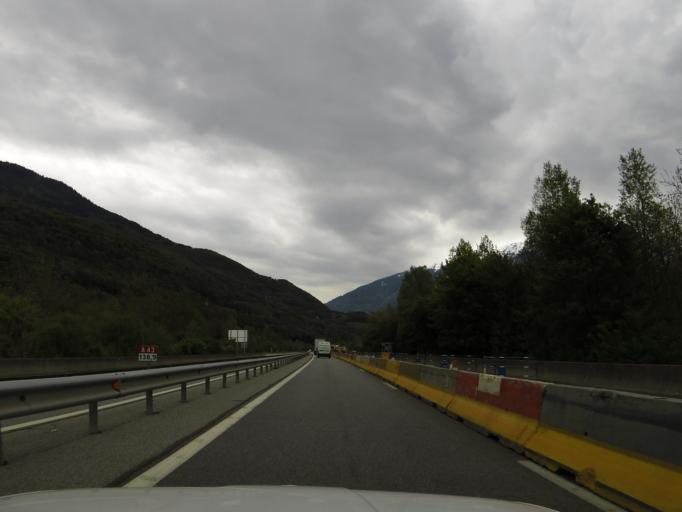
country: FR
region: Rhone-Alpes
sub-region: Departement de la Savoie
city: Aiton
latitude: 45.4933
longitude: 6.2970
